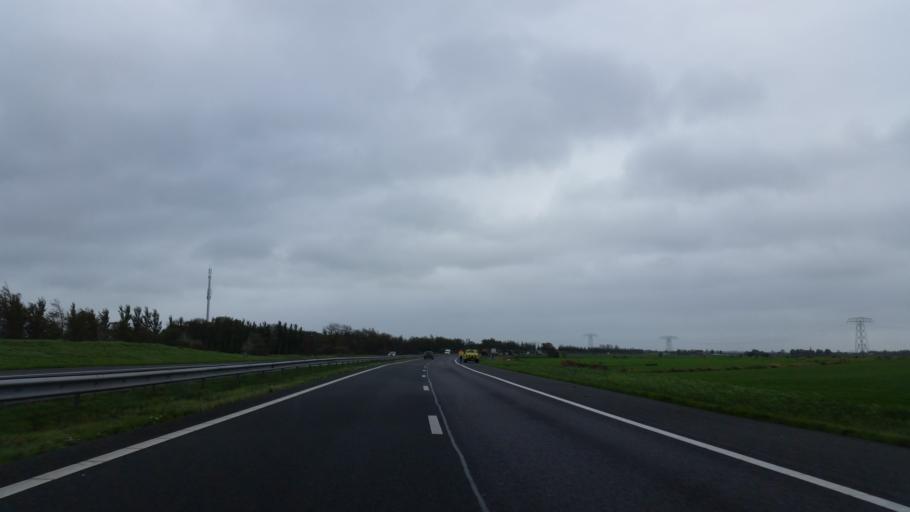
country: NL
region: Friesland
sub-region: Gemeente Boarnsterhim
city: Nes
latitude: 53.0248
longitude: 5.8629
